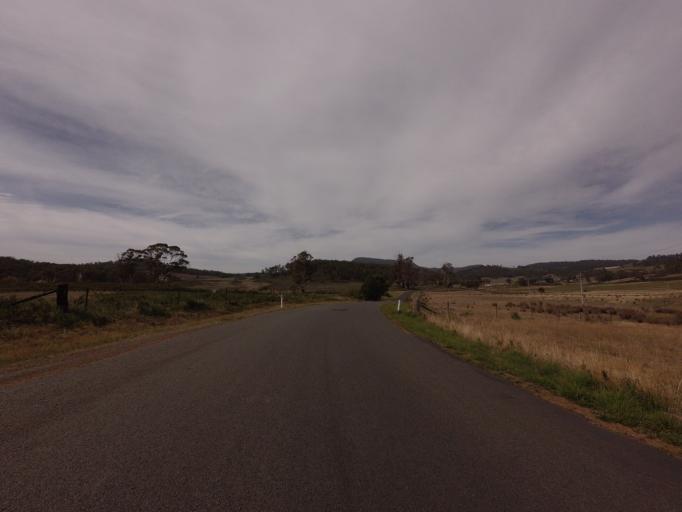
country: AU
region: Tasmania
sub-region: Sorell
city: Sorell
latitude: -42.4540
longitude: 147.5743
